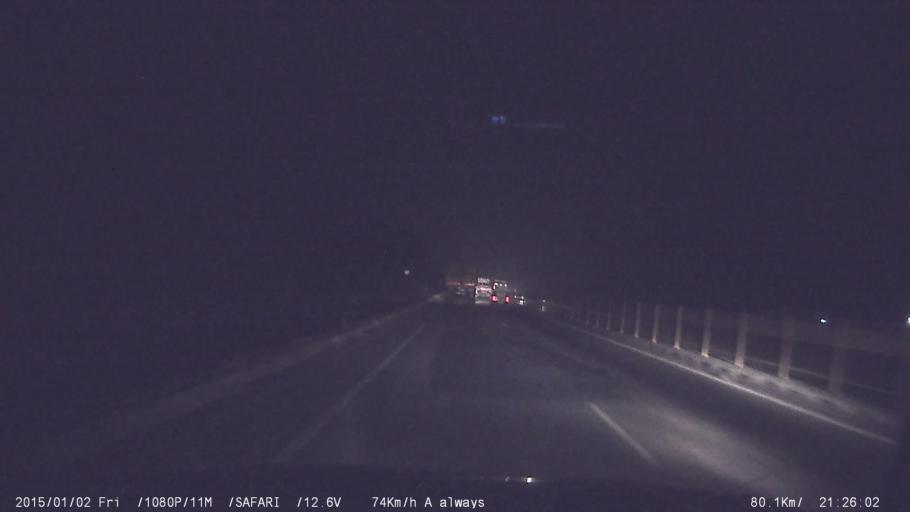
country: IN
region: Tamil Nadu
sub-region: Kancheepuram
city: Kanchipuram
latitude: 12.8983
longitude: 79.5458
